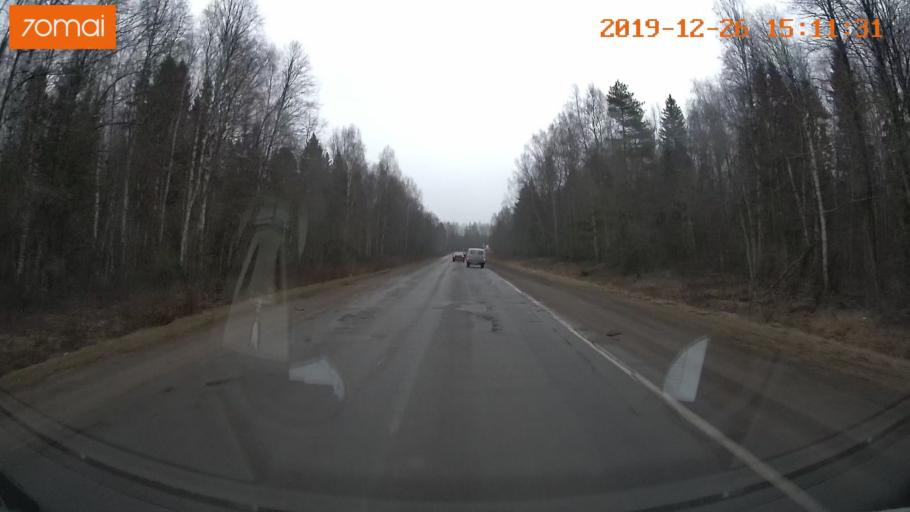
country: RU
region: Jaroslavl
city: Rybinsk
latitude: 58.1340
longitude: 38.8630
